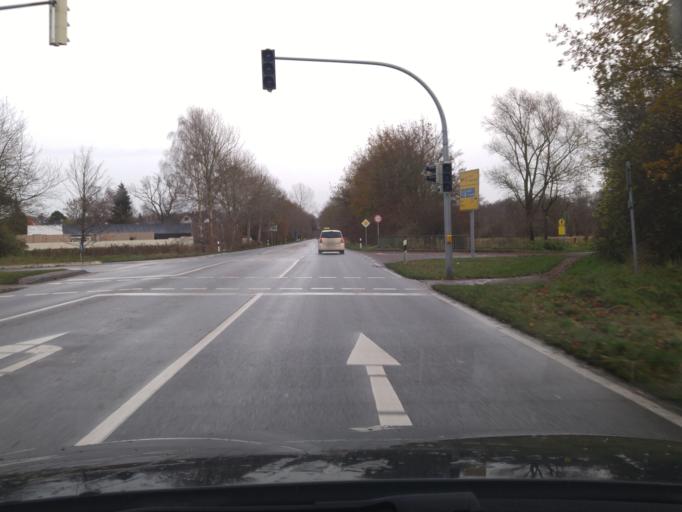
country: DE
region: Schleswig-Holstein
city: Timmendorfer Strand
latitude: 53.9890
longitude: 10.7919
